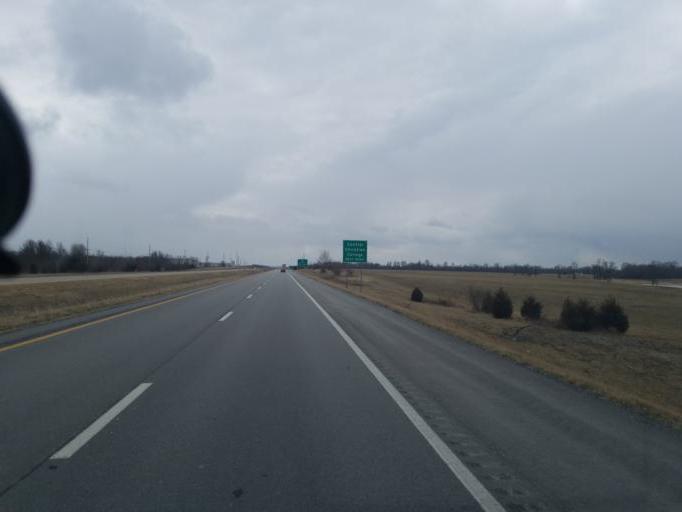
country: US
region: Missouri
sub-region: Randolph County
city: Moberly
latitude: 39.4064
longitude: -92.4126
